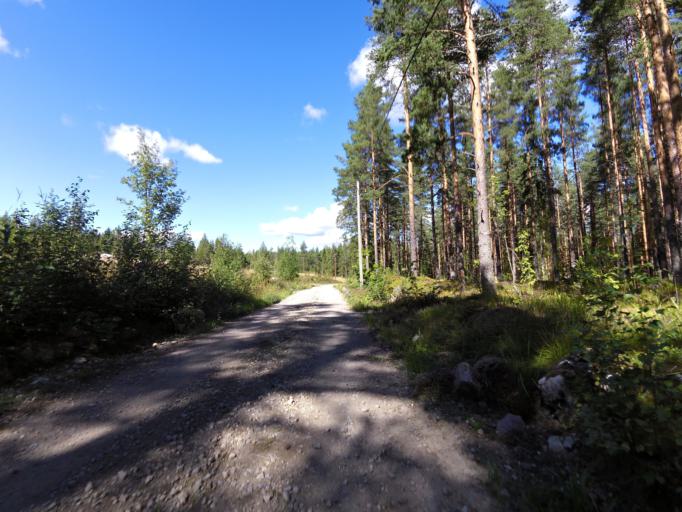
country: SE
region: Gaevleborg
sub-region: Gavle Kommun
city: Valbo
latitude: 60.7585
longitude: 16.9628
